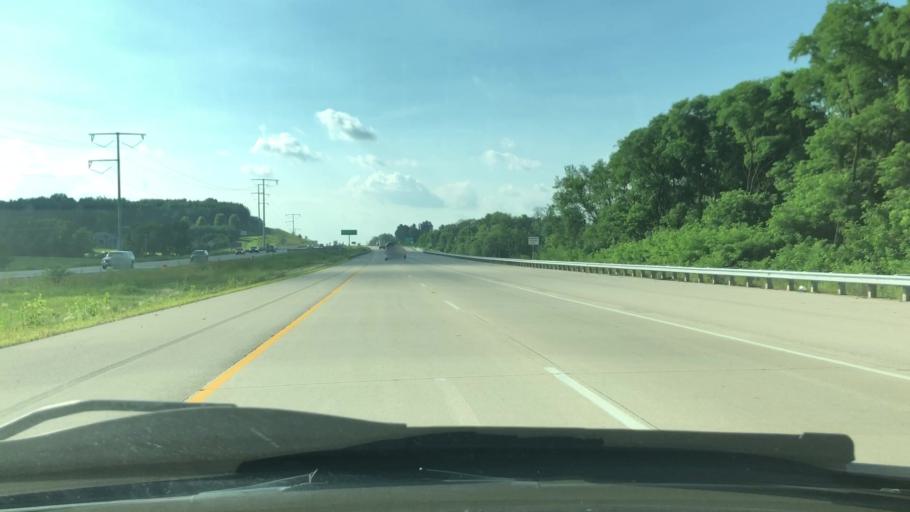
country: US
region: Wisconsin
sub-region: Dane County
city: McFarland
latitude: 43.0267
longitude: -89.2533
